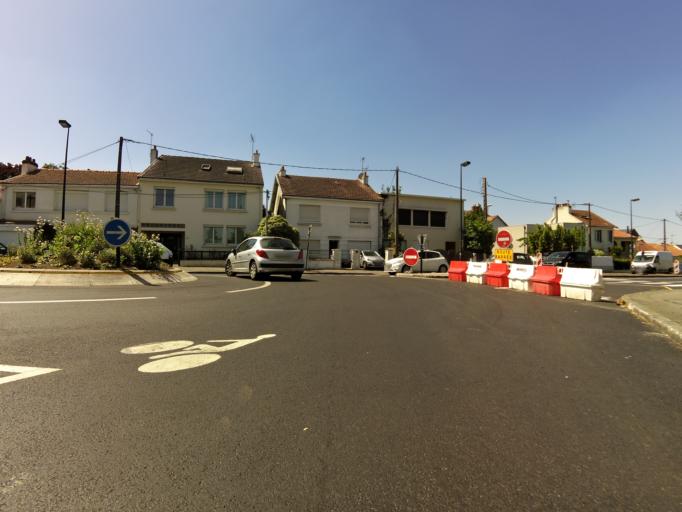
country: FR
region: Pays de la Loire
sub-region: Departement de la Loire-Atlantique
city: Nantes
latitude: 47.2398
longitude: -1.5845
